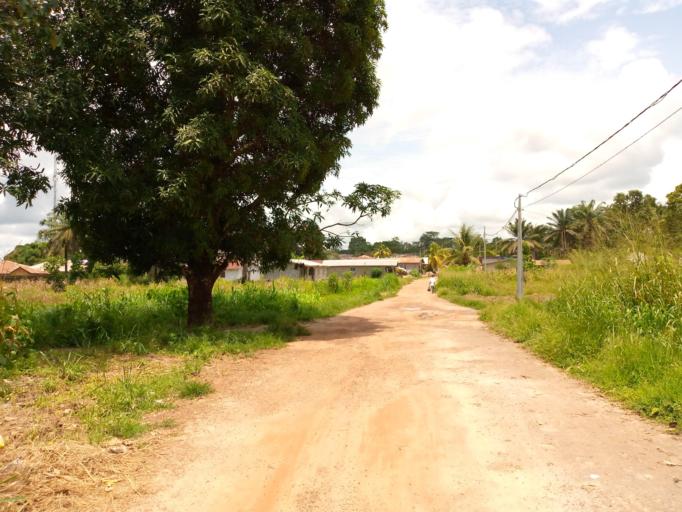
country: SL
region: Northern Province
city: Magburaka
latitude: 8.7200
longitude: -11.9478
